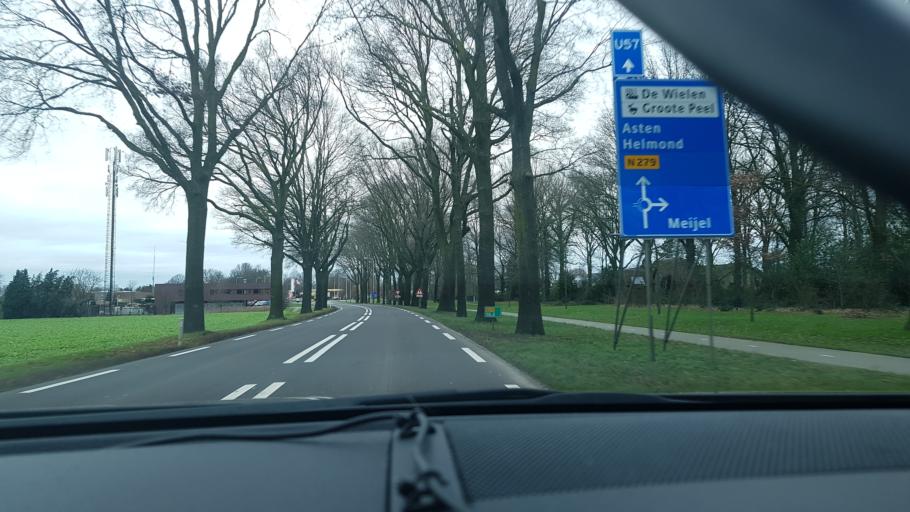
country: NL
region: Limburg
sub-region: Gemeente Leudal
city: Heythuysen
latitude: 51.3403
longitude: 5.8823
